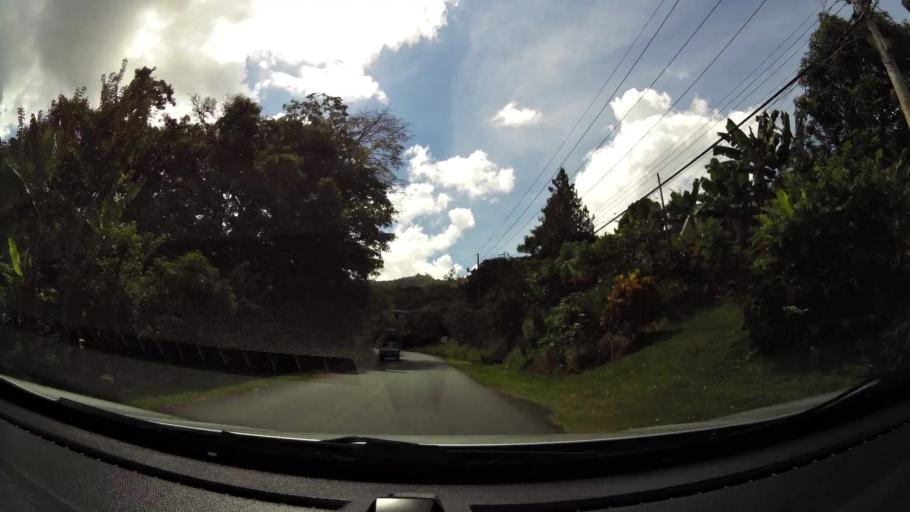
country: CR
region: San Jose
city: San Isidro
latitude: 9.3470
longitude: -83.7363
